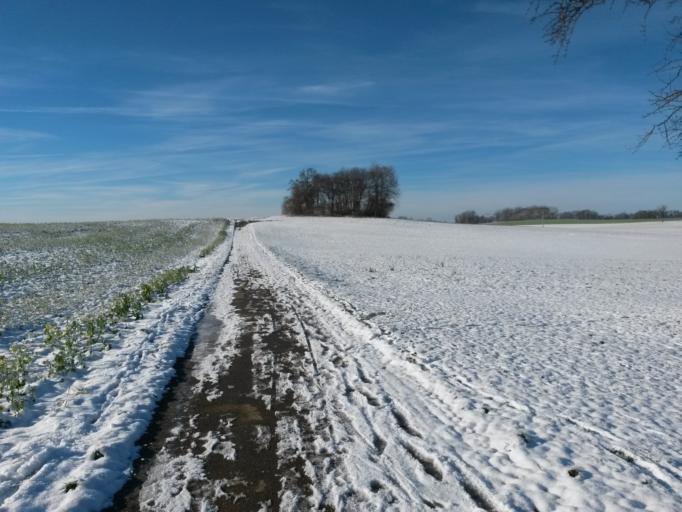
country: DE
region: Baden-Wuerttemberg
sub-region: Regierungsbezirk Stuttgart
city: Bad Uberkingen
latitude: 48.6147
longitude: 9.7778
